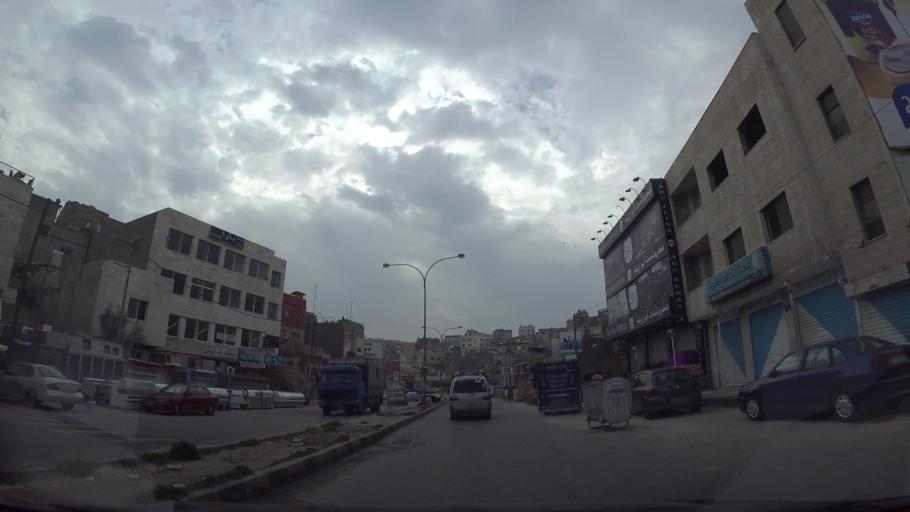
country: JO
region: Amman
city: Amman
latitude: 31.9635
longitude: 35.9285
